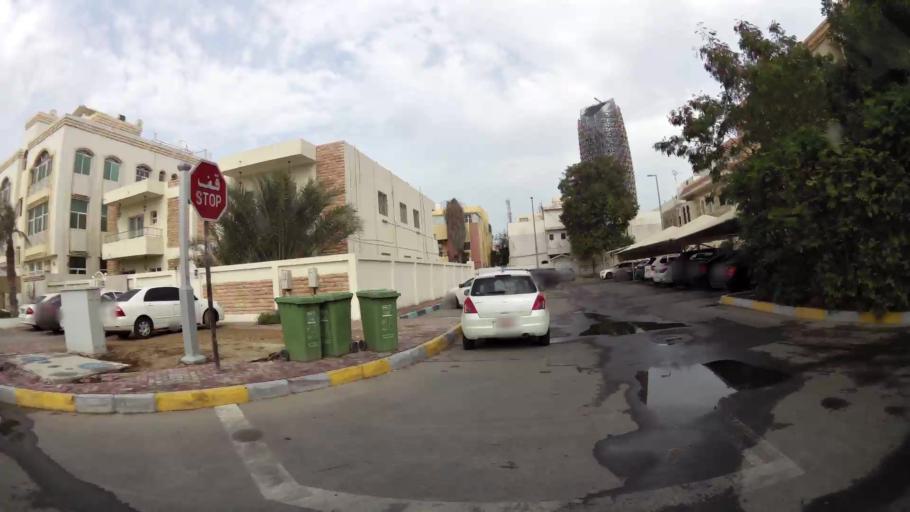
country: AE
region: Abu Dhabi
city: Abu Dhabi
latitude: 24.4530
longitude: 54.4031
